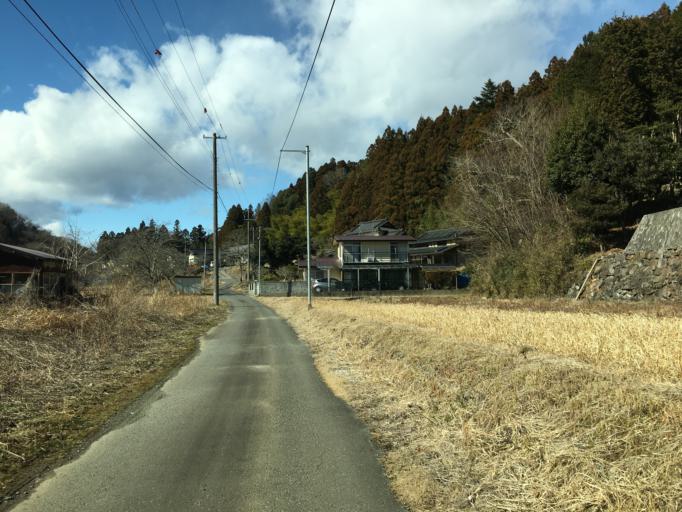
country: JP
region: Fukushima
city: Iwaki
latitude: 37.0098
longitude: 140.7928
